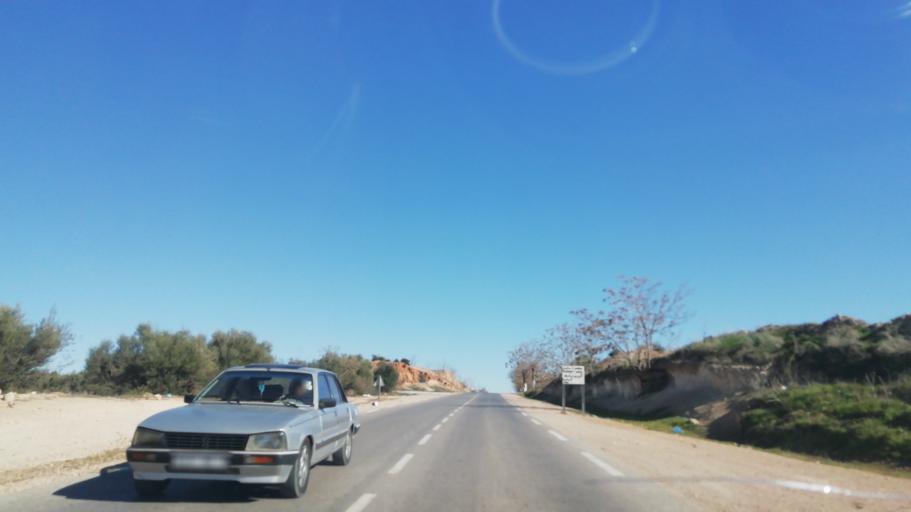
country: DZ
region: Tlemcen
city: Beni Mester
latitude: 34.8245
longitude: -1.5670
